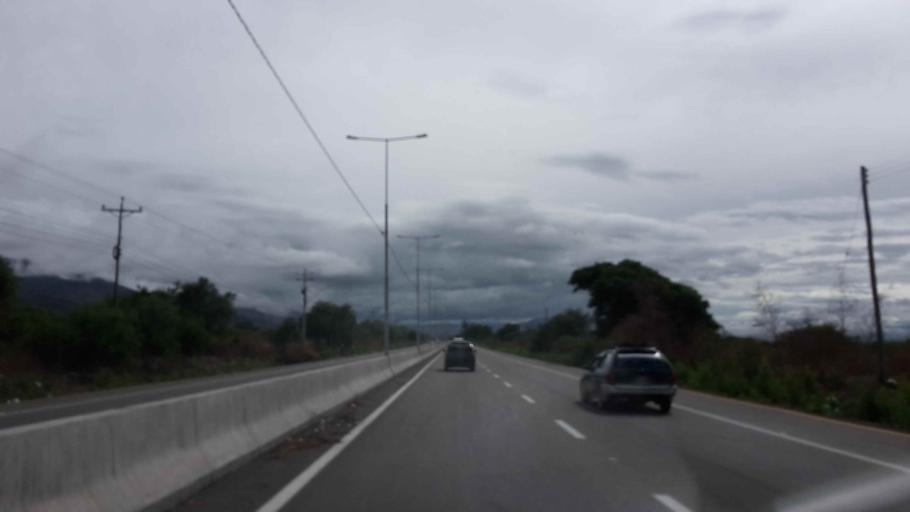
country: BO
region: Cochabamba
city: Tarata
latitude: -17.5435
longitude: -66.0019
